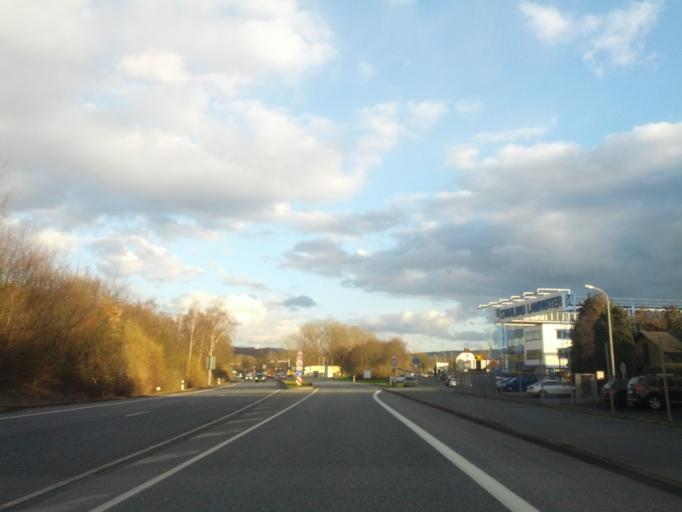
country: DE
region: Hesse
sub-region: Regierungsbezirk Kassel
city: Lohfelden
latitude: 51.2930
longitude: 9.5607
